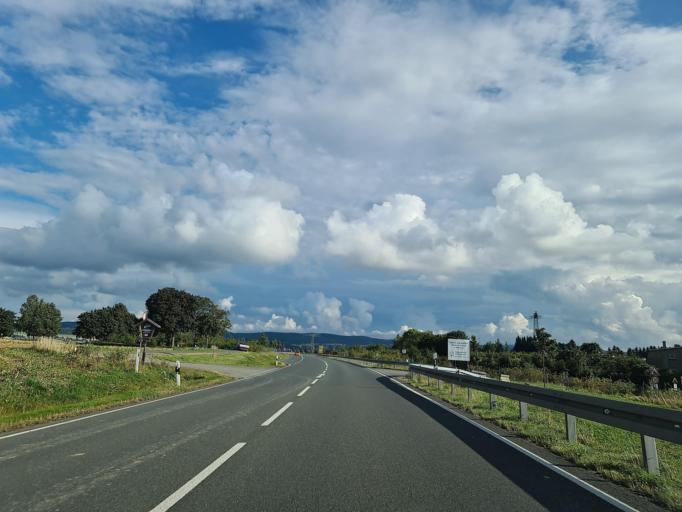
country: DE
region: Saxony
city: Auerbach
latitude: 50.5272
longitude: 12.3773
